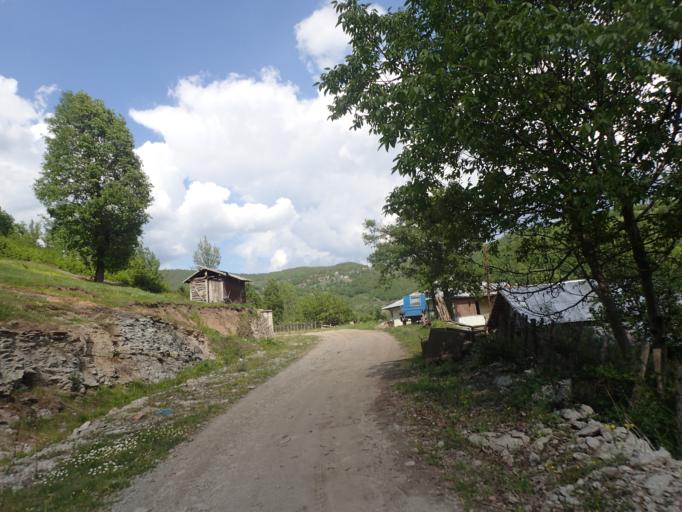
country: TR
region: Ordu
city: Akkus
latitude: 40.8150
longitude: 36.9368
